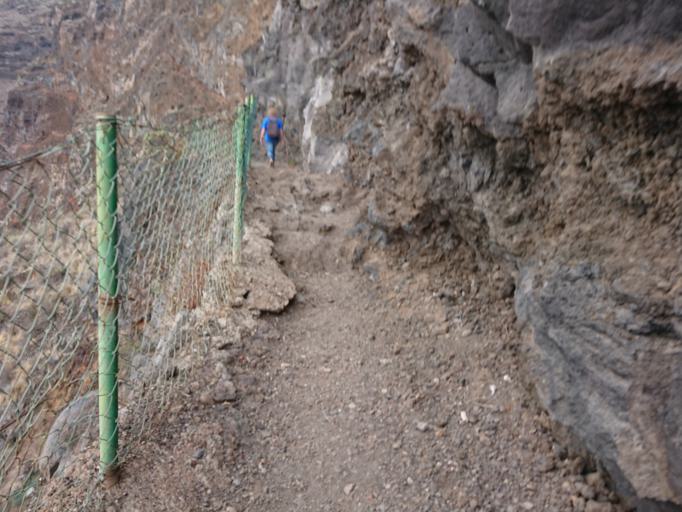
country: ES
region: Canary Islands
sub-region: Provincia de Santa Cruz de Tenerife
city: Tijarafe
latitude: 28.7183
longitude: -17.9783
